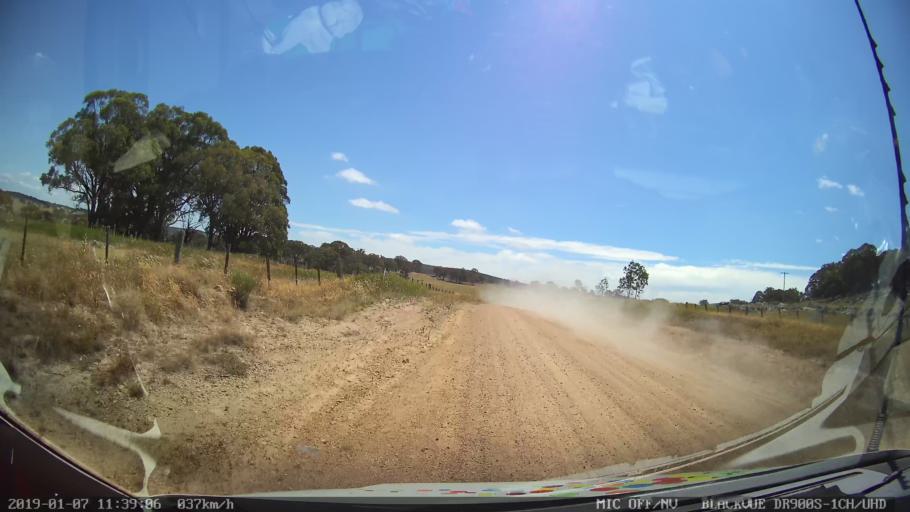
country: AU
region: New South Wales
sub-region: Armidale Dumaresq
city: Armidale
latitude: -30.3687
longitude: 151.5746
